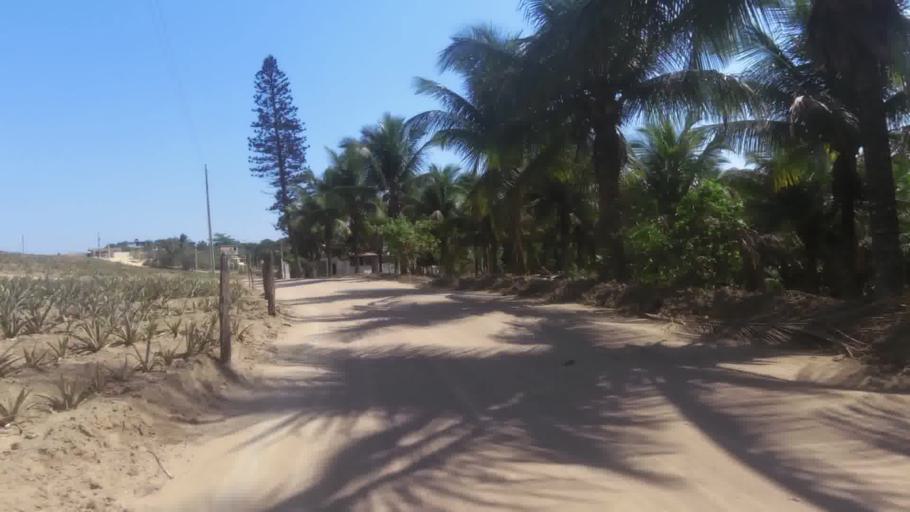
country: BR
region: Espirito Santo
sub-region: Marataizes
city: Marataizes
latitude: -21.1055
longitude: -40.8577
